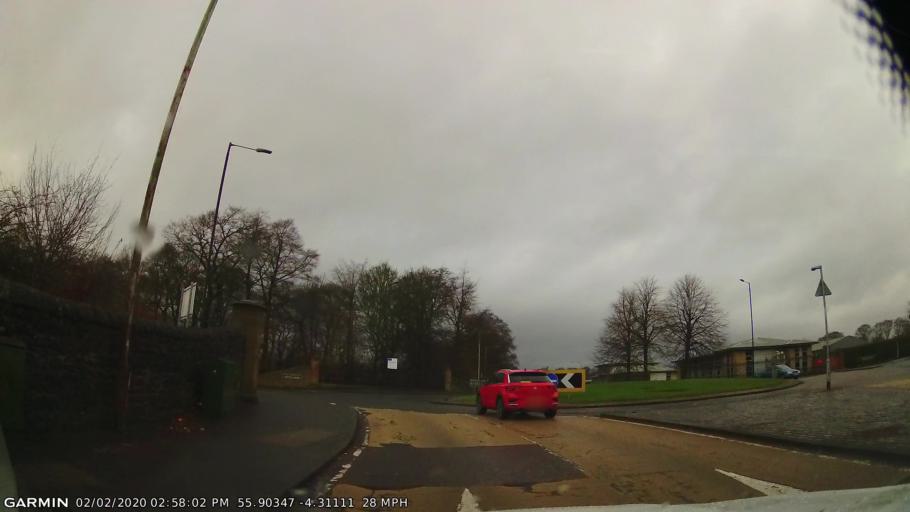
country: GB
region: Scotland
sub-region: East Dunbartonshire
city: Bearsden
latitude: 55.9035
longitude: -4.3111
